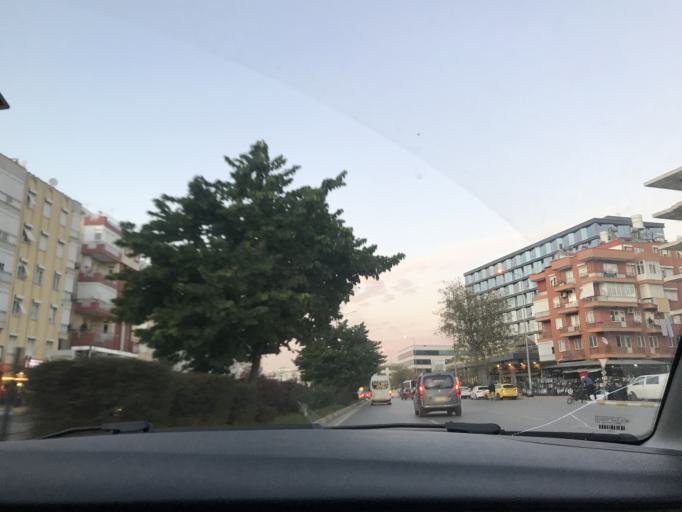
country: TR
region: Antalya
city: Antalya
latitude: 36.8992
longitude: 30.7155
